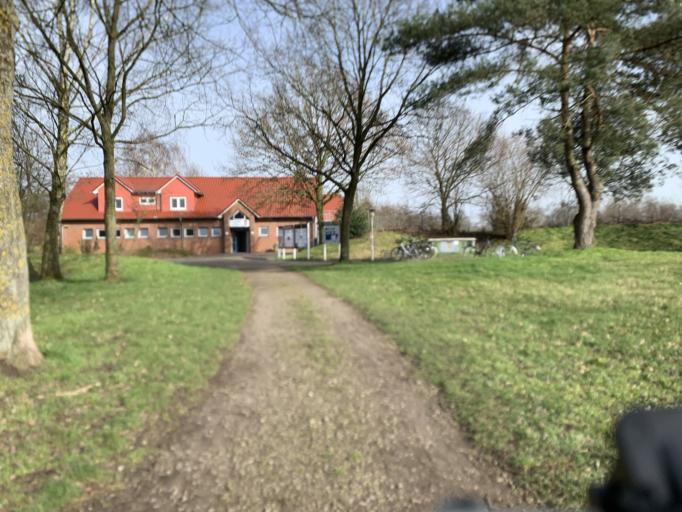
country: DE
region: Lower Saxony
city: Hassel
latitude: 52.6787
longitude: 8.8297
